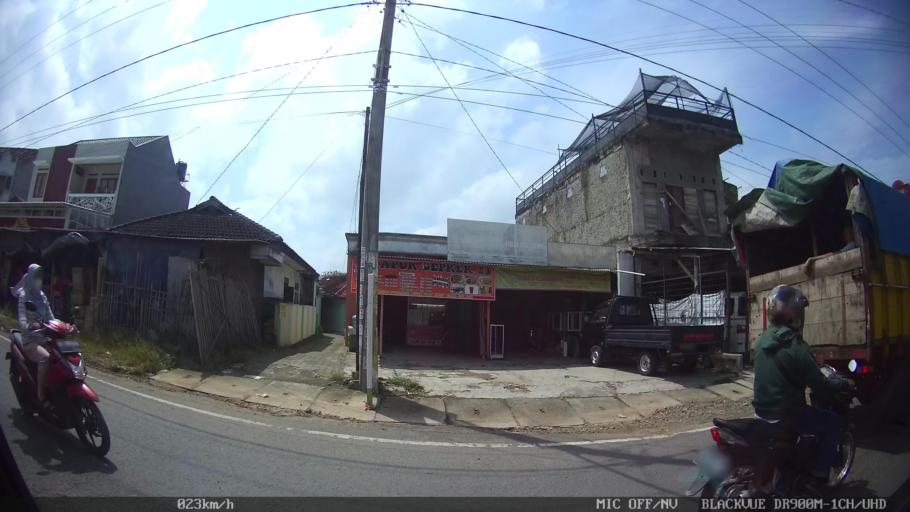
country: ID
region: Lampung
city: Kedaton
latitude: -5.3494
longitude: 105.2935
